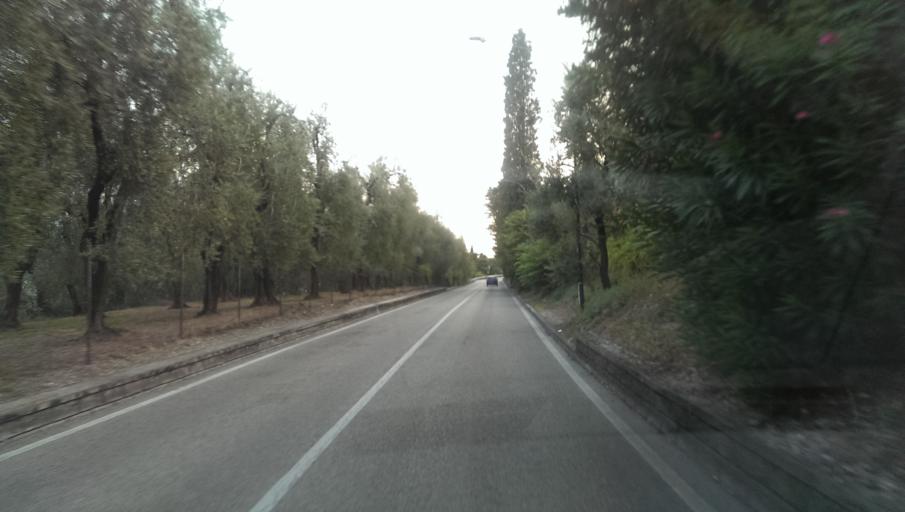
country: IT
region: Lombardy
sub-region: Provincia di Brescia
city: Limone sul Garda
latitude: 45.8039
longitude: 10.7873
